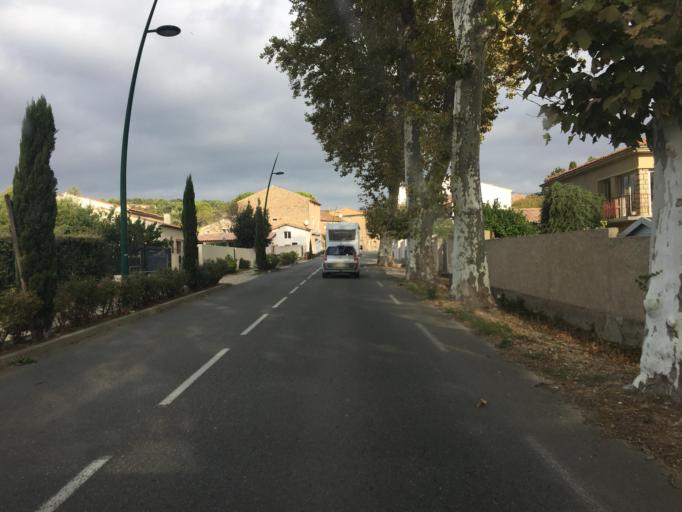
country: FR
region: Languedoc-Roussillon
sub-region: Departement de l'Herault
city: Nebian
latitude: 43.6049
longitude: 3.4369
